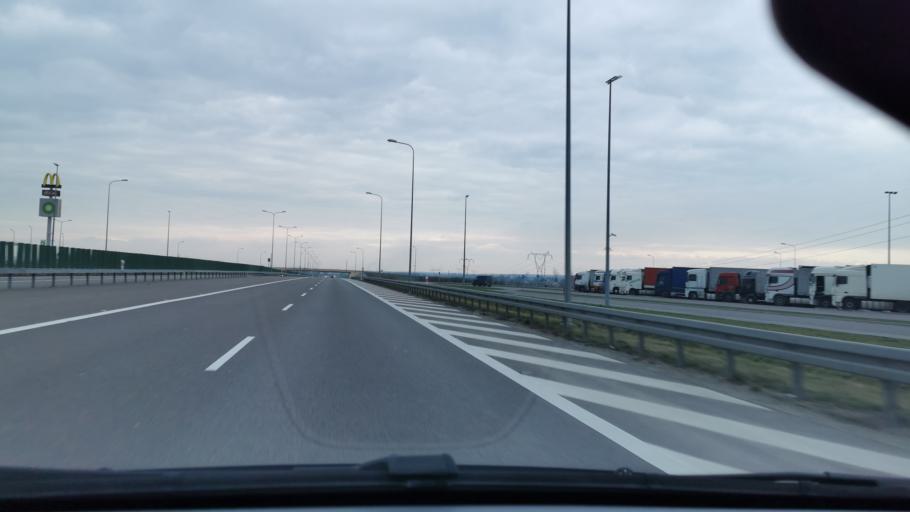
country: PL
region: Lublin Voivodeship
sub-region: Powiat pulawski
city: Markuszow
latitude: 51.3894
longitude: 22.2489
